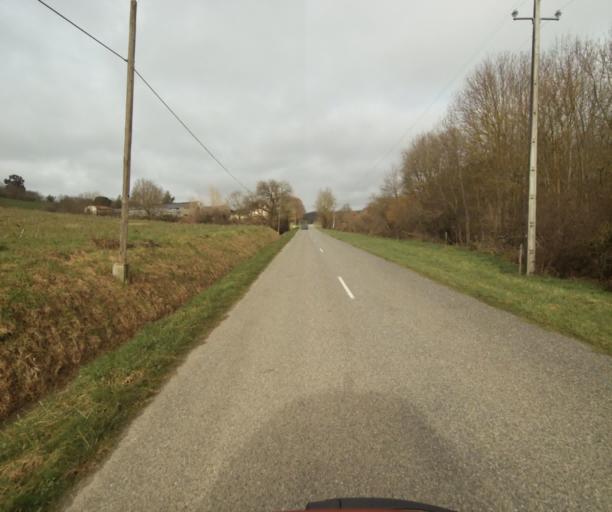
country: FR
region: Midi-Pyrenees
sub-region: Departement de l'Ariege
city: Pamiers
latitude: 43.1383
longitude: 1.5358
